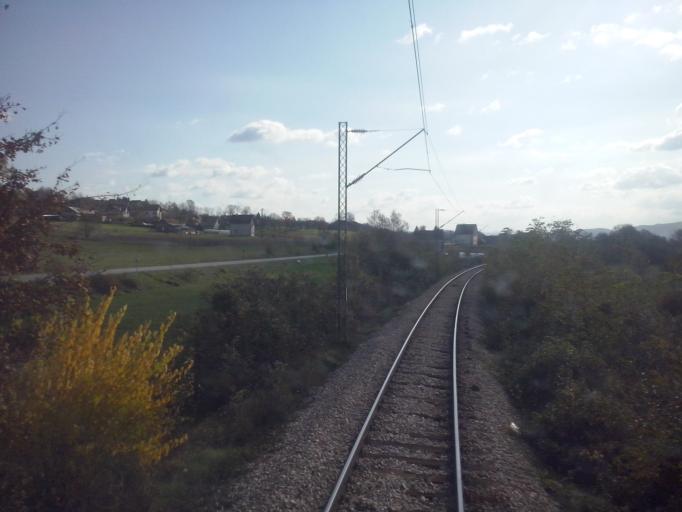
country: RS
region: Central Serbia
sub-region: Zlatiborski Okrug
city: Pozega
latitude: 43.8693
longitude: 20.0088
